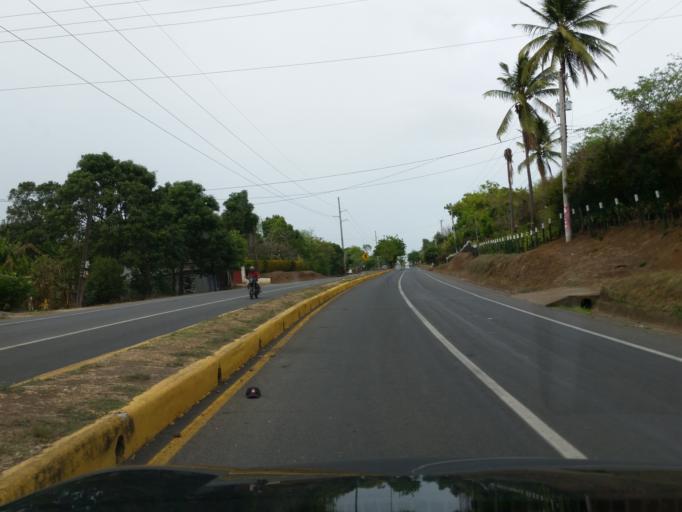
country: NI
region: Masaya
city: Masaya
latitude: 11.9761
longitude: -86.0348
